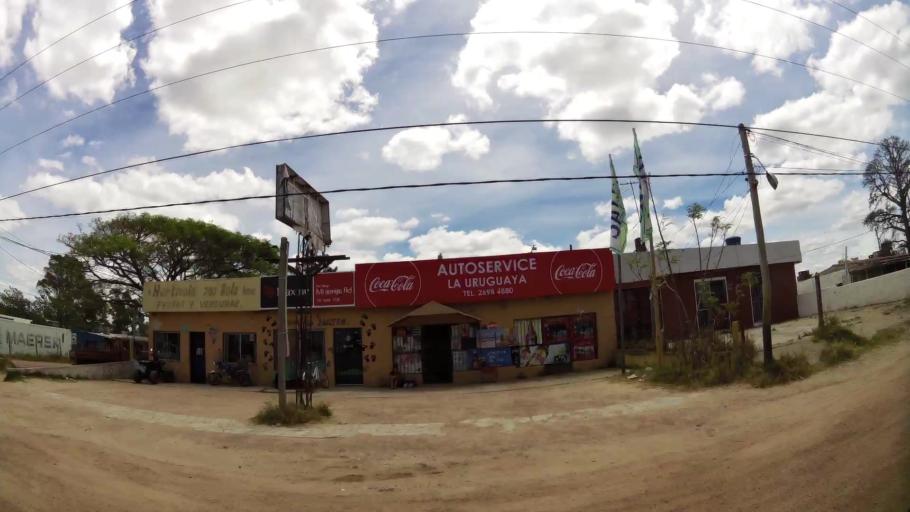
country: UY
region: Canelones
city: Pando
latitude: -34.8075
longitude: -55.9328
